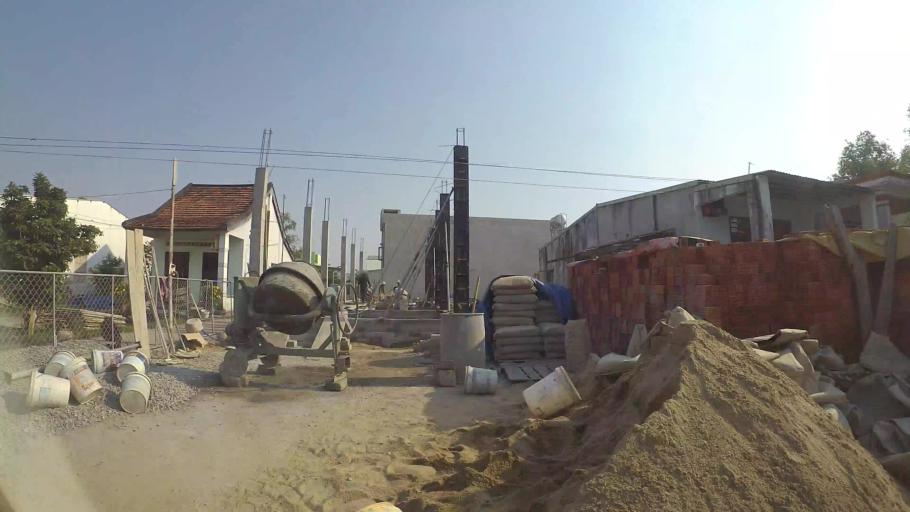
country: VN
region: Quang Nam
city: Quang Nam
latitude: 15.9489
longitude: 108.2585
